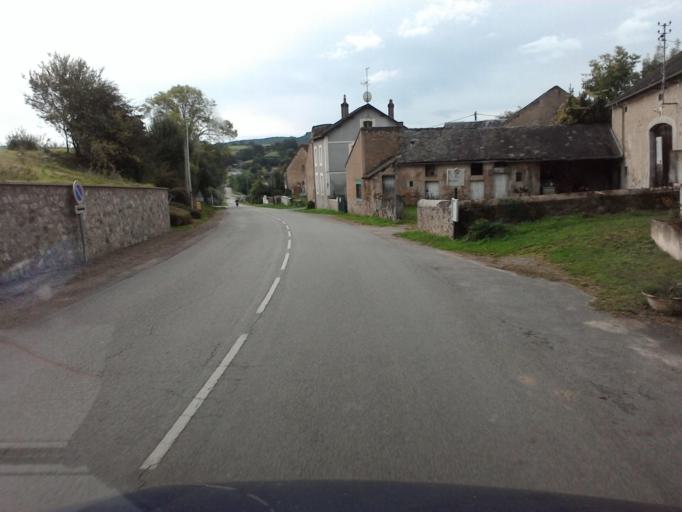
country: FR
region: Bourgogne
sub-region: Departement de la Nievre
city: Lormes
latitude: 47.2325
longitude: 3.8236
